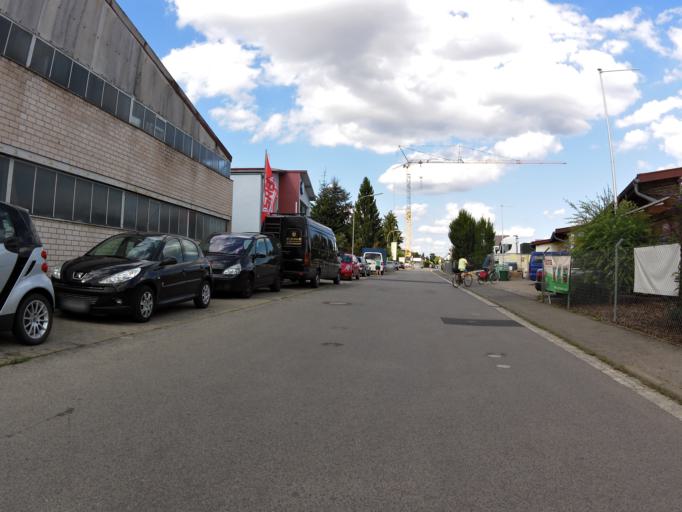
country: DE
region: Bavaria
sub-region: Regierungsbezirk Unterfranken
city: Bergrheinfeld
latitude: 50.0090
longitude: 10.1848
